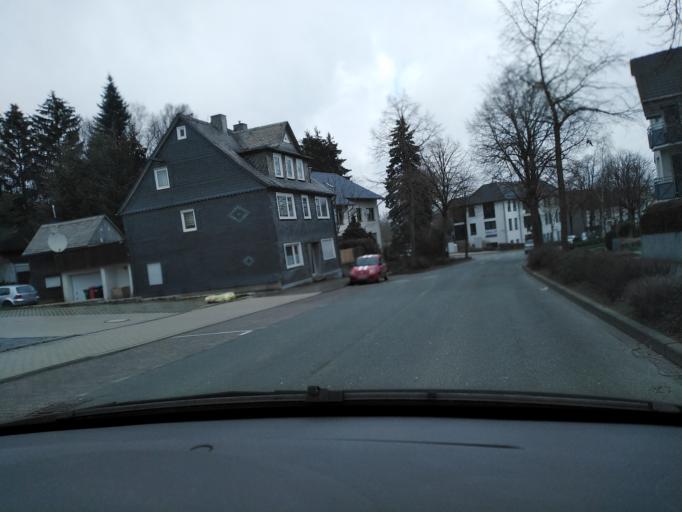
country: DE
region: North Rhine-Westphalia
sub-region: Regierungsbezirk Arnsberg
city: Brilon
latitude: 51.4007
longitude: 8.5687
